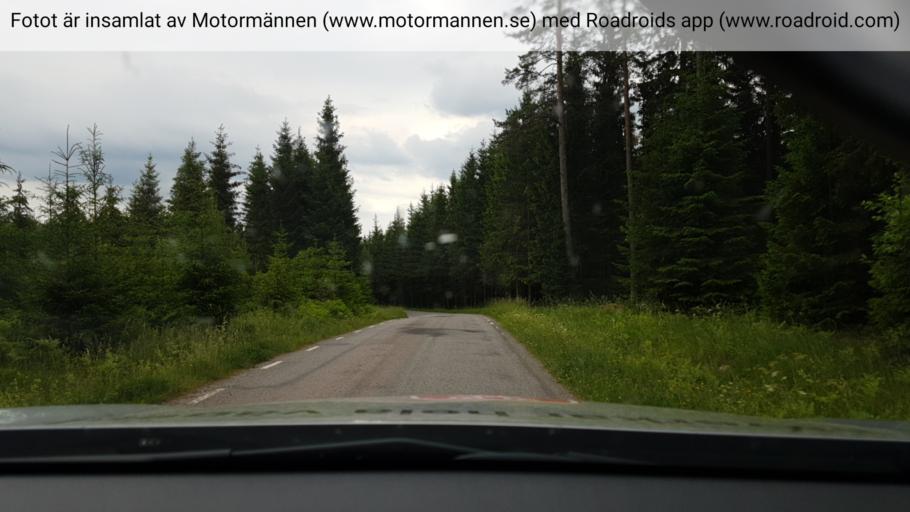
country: SE
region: Joenkoeping
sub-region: Mullsjo Kommun
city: Mullsjoe
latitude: 57.9547
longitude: 13.7078
